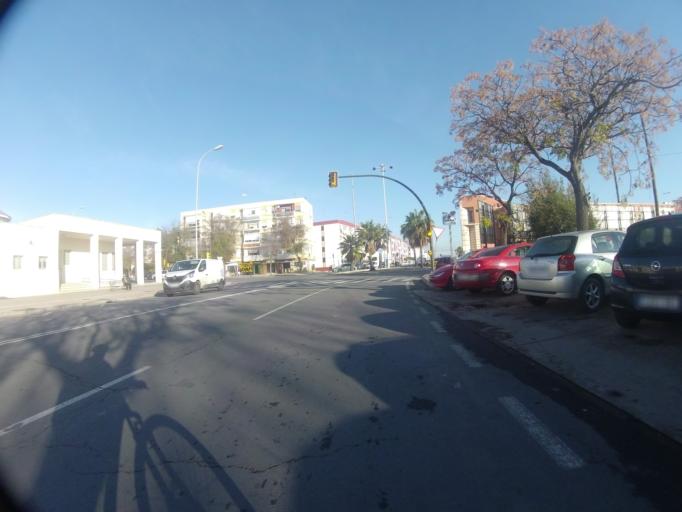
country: ES
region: Andalusia
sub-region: Provincia de Huelva
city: Huelva
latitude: 37.2794
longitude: -6.9365
